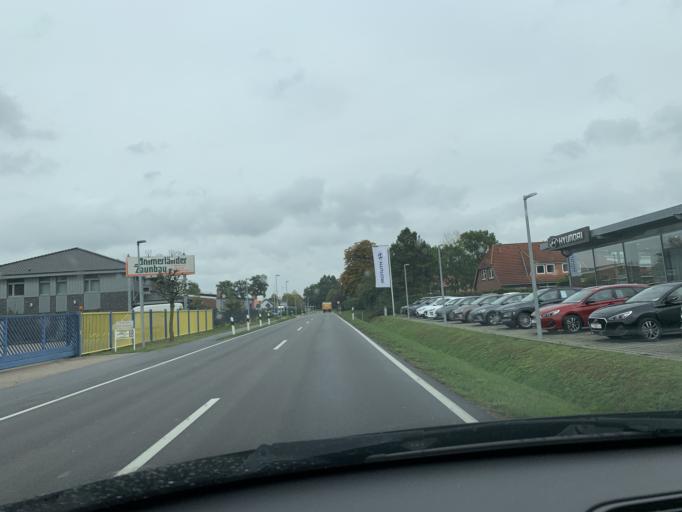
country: DE
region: Lower Saxony
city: Bad Zwischenahn
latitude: 53.1734
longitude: 8.0683
